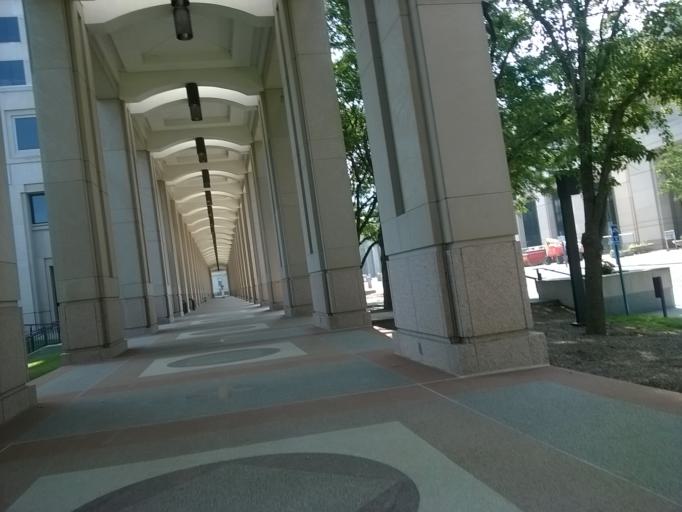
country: US
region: Indiana
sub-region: Marion County
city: Indianapolis
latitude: 39.7689
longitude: -86.1664
